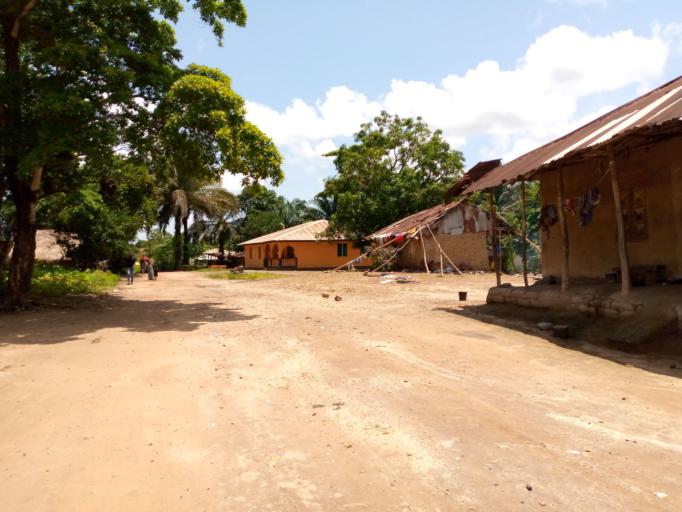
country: SL
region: Northern Province
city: Magburaka
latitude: 8.7165
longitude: -11.9594
